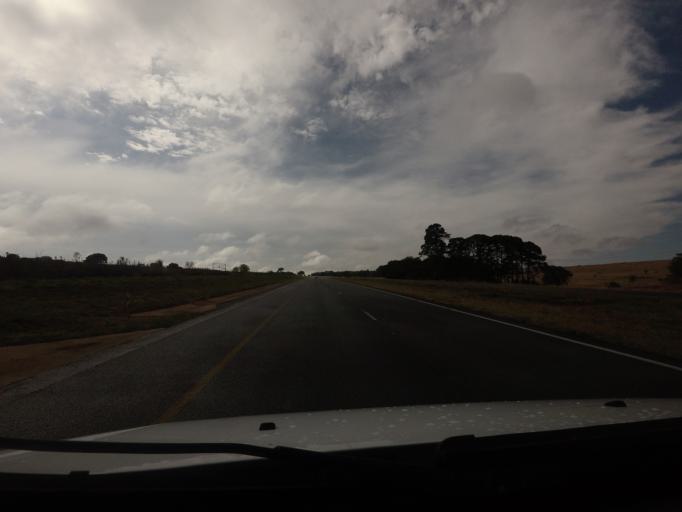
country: ZA
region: Gauteng
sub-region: City of Tshwane Metropolitan Municipality
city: Cullinan
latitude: -25.7916
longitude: 28.4934
